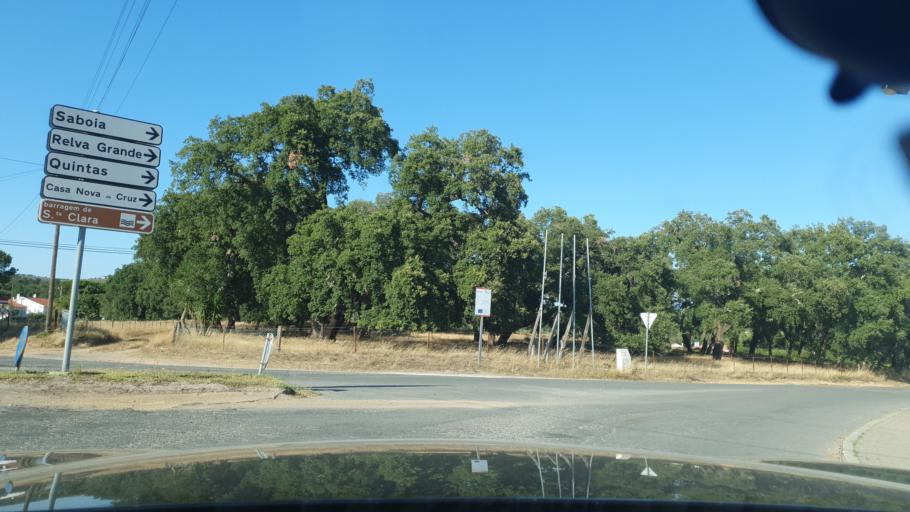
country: PT
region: Beja
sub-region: Odemira
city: Sao Teotonio
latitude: 37.5122
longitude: -8.7030
